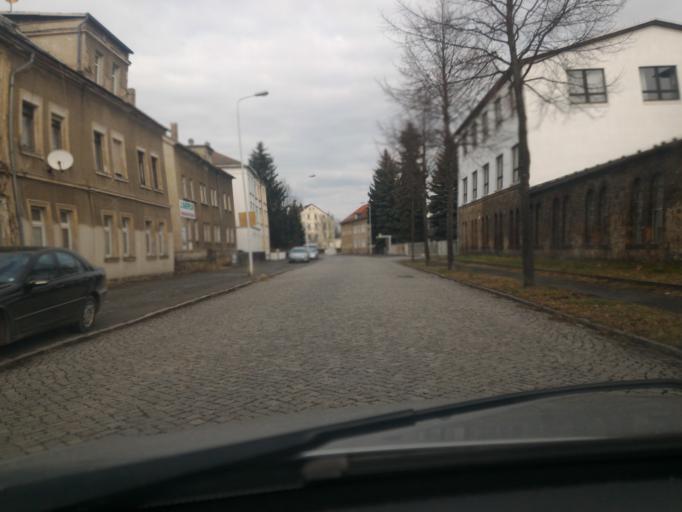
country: DE
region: Saxony
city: Zittau
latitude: 50.8837
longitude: 14.8141
